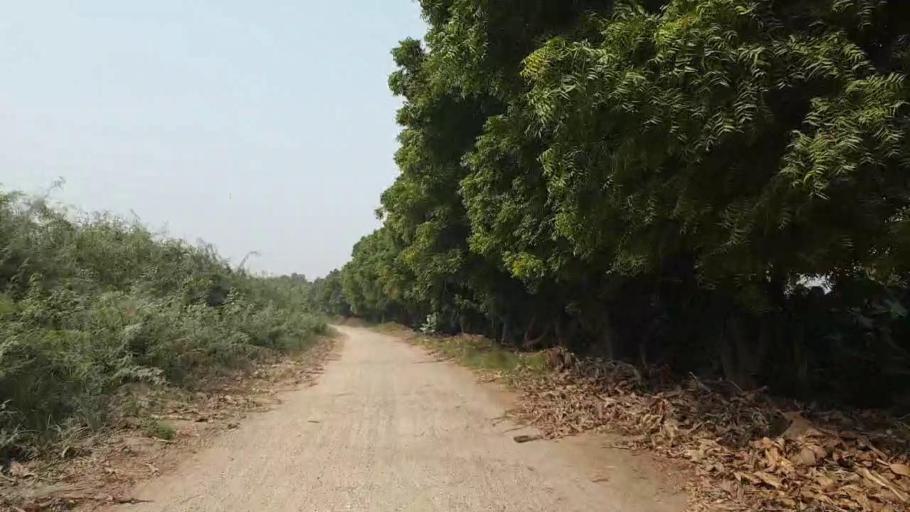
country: PK
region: Sindh
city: Tando Muhammad Khan
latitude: 25.1876
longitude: 68.5955
